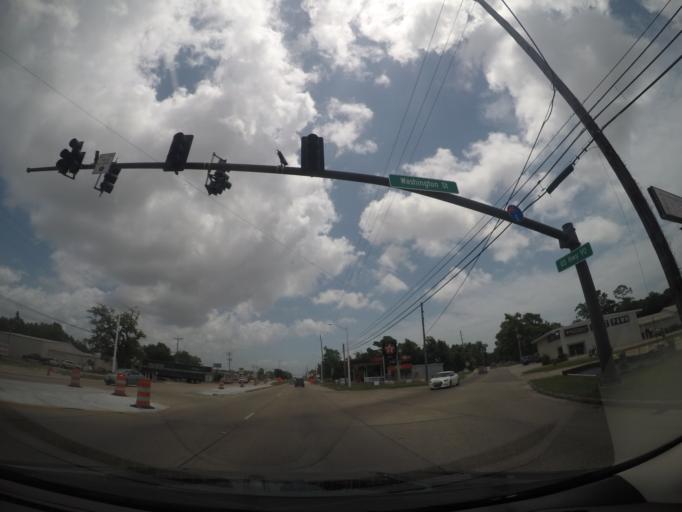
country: US
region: Mississippi
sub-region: Hancock County
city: Bay Saint Louis
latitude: 30.3125
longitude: -89.3592
